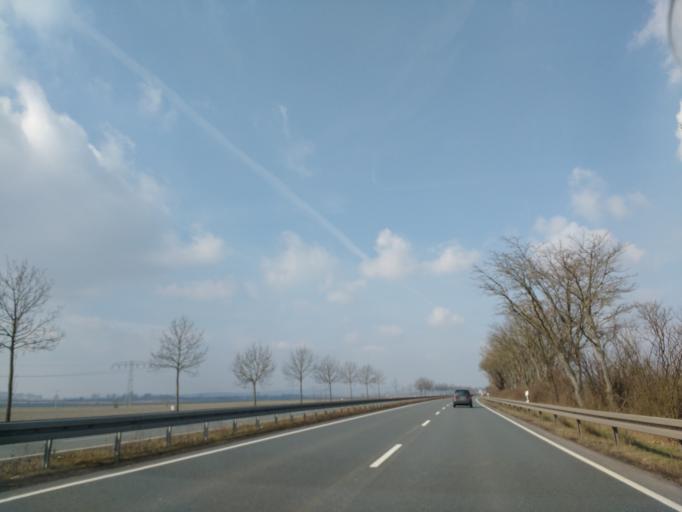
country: DE
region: Saxony-Anhalt
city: Wansleben
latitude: 51.4726
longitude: 11.7328
